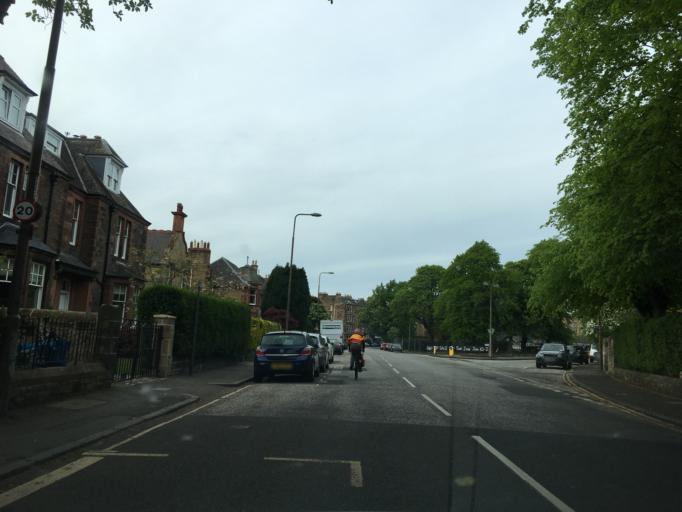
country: GB
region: Scotland
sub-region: Edinburgh
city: Edinburgh
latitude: 55.9341
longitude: -3.2231
